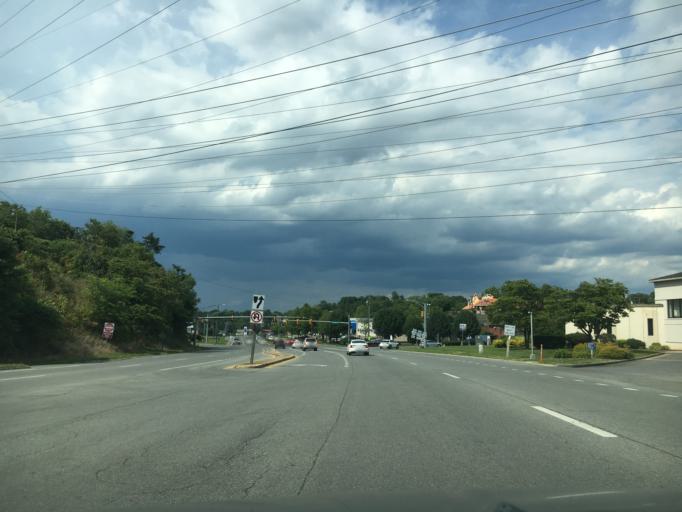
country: US
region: Virginia
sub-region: Roanoke County
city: Cave Spring
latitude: 37.2289
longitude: -80.0090
